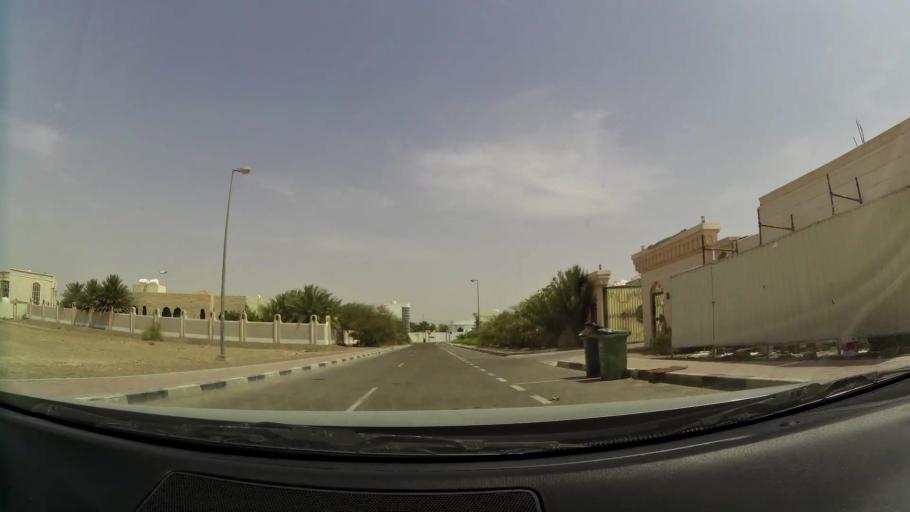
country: AE
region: Abu Dhabi
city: Al Ain
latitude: 24.1757
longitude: 55.7171
